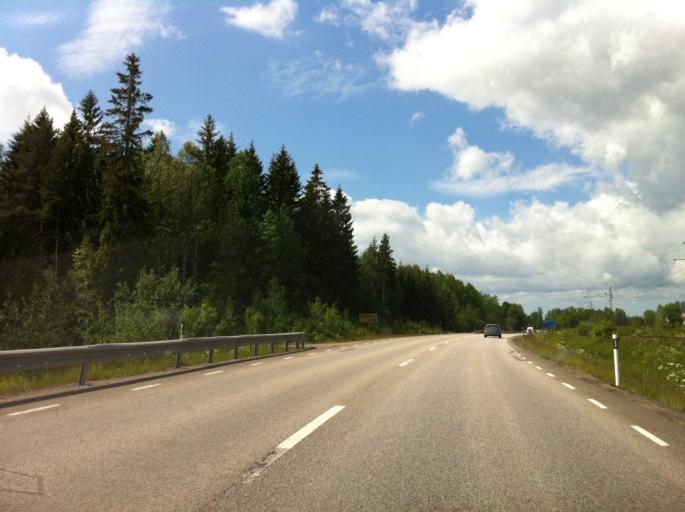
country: SE
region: Vaermland
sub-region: Saffle Kommun
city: Saeffle
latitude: 59.1563
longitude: 12.9852
